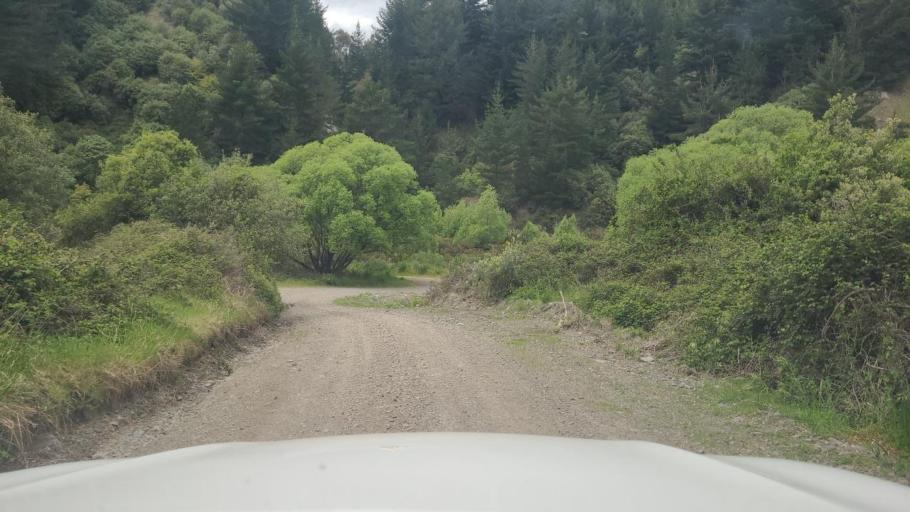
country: NZ
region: Hawke's Bay
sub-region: Napier City
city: Taradale
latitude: -39.1850
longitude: 176.6338
